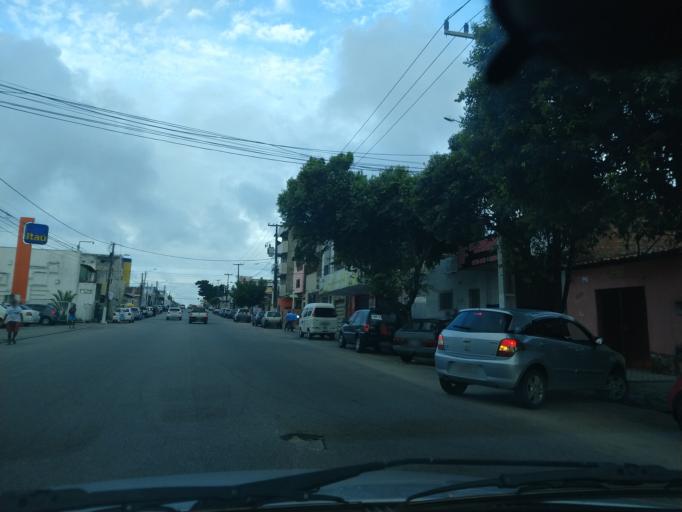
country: BR
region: Rio Grande do Norte
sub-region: Natal
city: Natal
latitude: -5.8008
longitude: -35.2228
